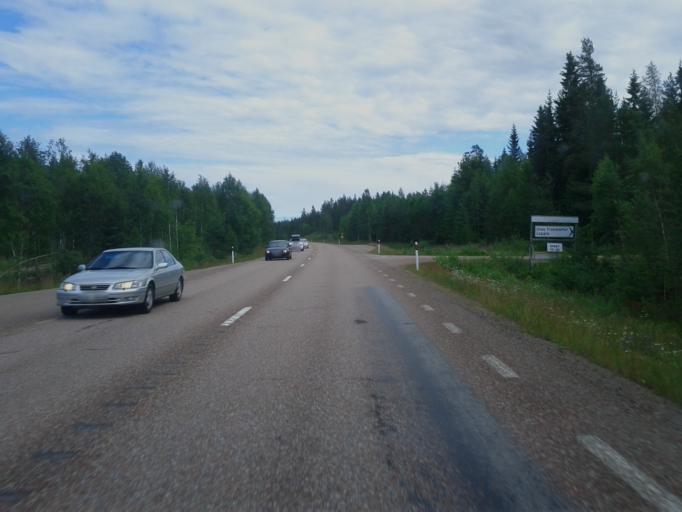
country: SE
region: Dalarna
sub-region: Faluns Kommun
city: Bjursas
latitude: 60.7863
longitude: 15.2898
